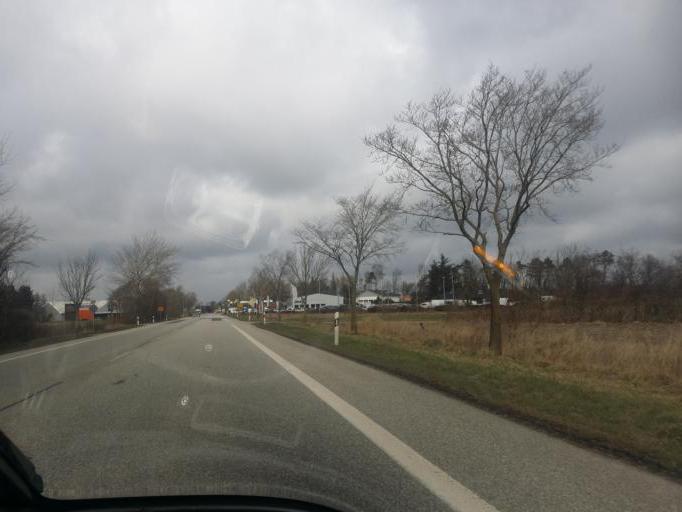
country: DE
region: Schleswig-Holstein
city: Bargum
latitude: 54.6805
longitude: 8.9562
